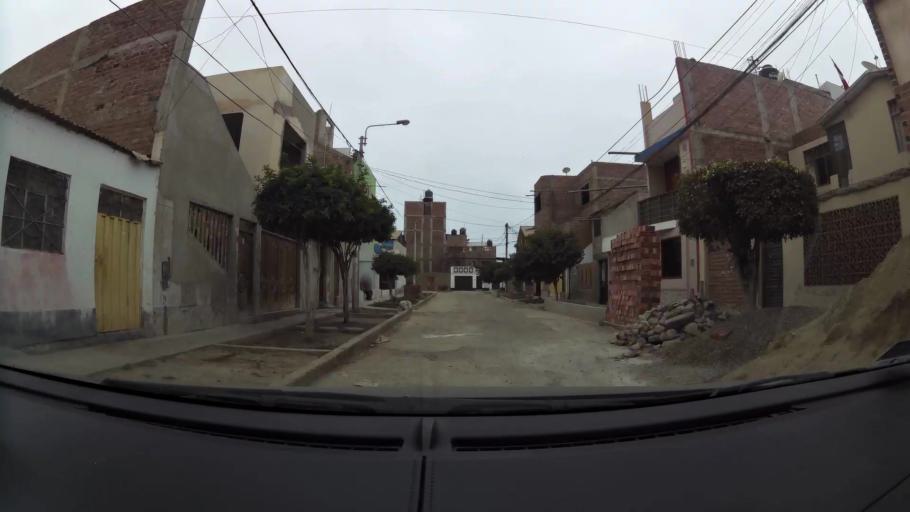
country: PE
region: La Libertad
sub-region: Provincia de Trujillo
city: Buenos Aires
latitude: -8.1409
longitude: -79.0543
